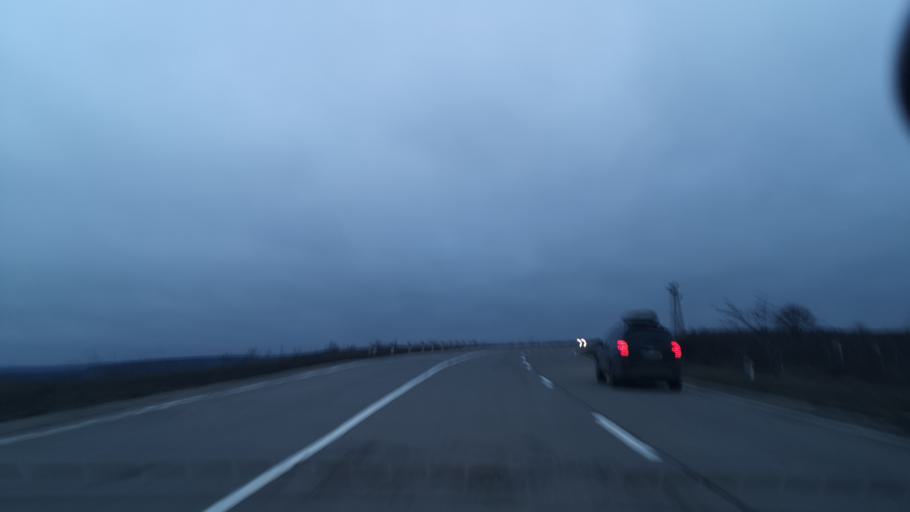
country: MD
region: Straseni
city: Straseni
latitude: 47.2941
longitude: 28.5748
